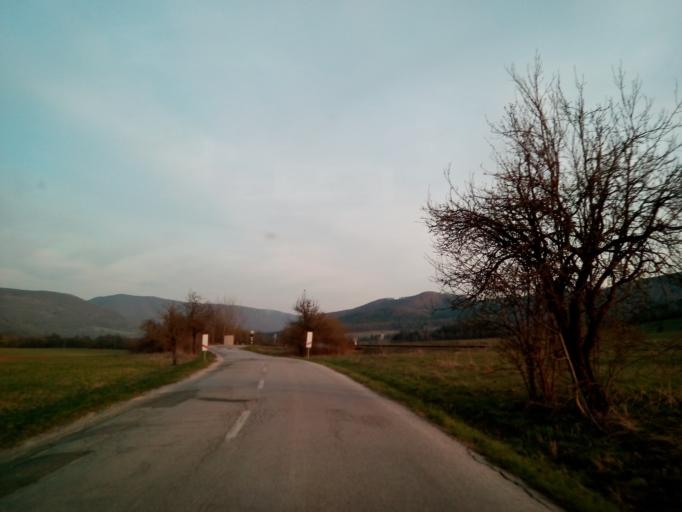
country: SK
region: Kosicky
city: Dobsina
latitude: 48.6955
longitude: 20.3137
